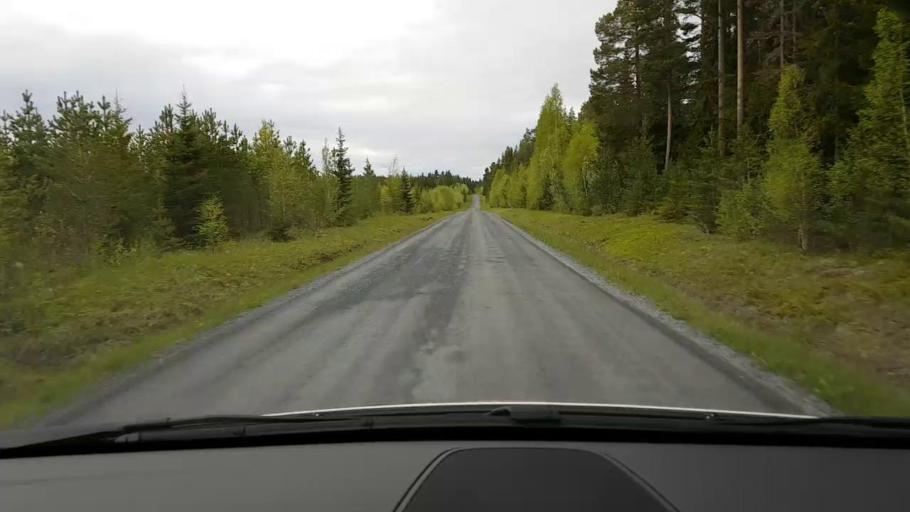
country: SE
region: Jaemtland
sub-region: Krokoms Kommun
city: Valla
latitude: 63.3069
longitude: 13.9978
